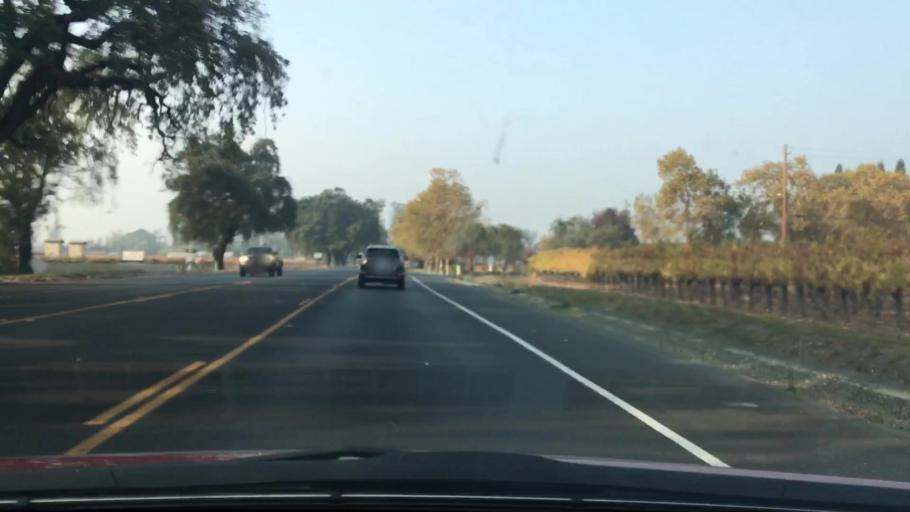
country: US
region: California
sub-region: Napa County
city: Saint Helena
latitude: 38.4722
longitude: -122.4325
